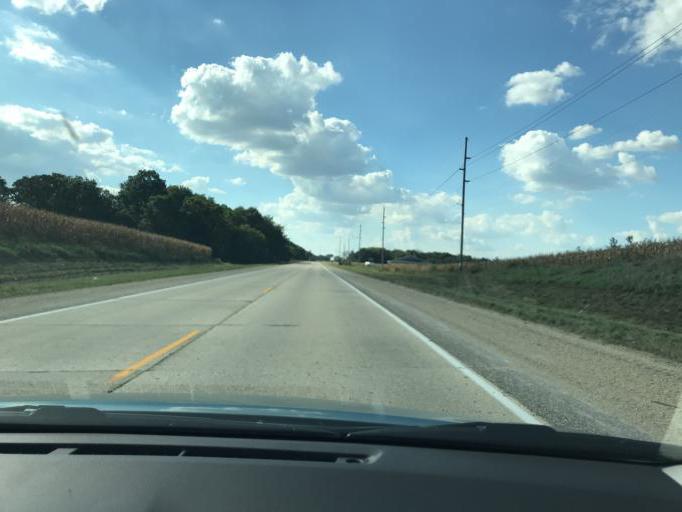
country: US
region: Wisconsin
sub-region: Rock County
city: Orfordville
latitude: 42.5443
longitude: -89.2606
